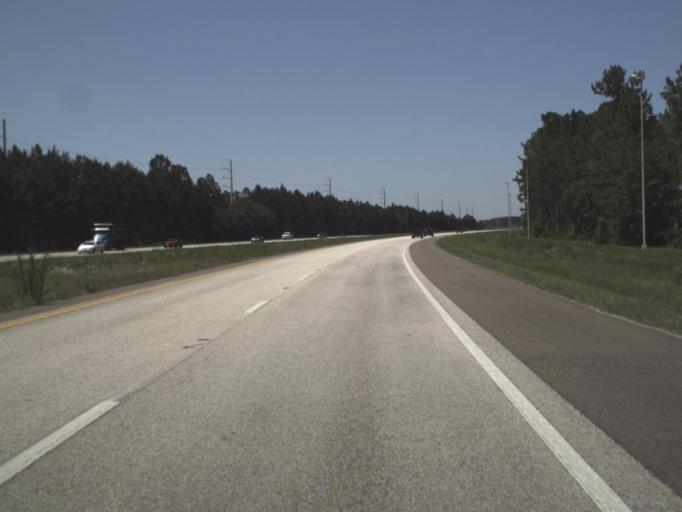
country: US
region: Florida
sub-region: Clay County
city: Bellair-Meadowbrook Terrace
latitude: 30.2296
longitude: -81.8432
